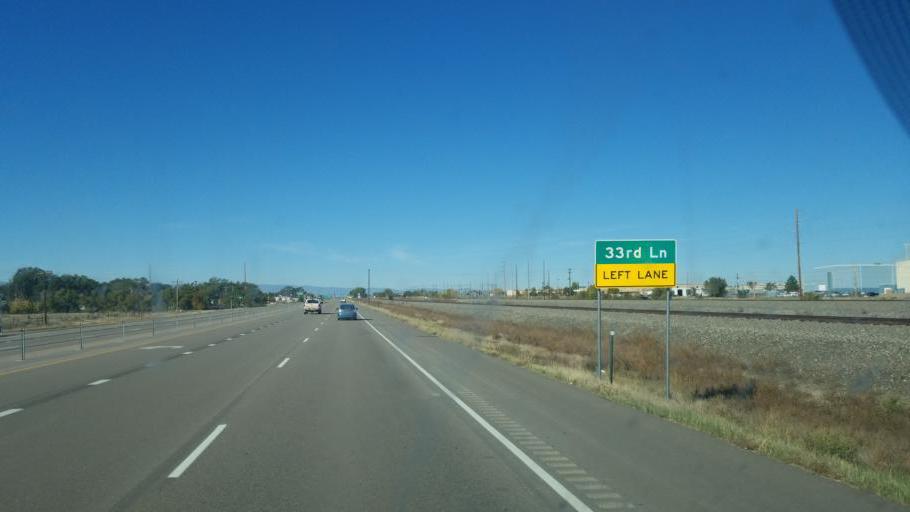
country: US
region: Colorado
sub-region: Pueblo County
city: Pueblo
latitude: 38.2756
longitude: -104.4839
